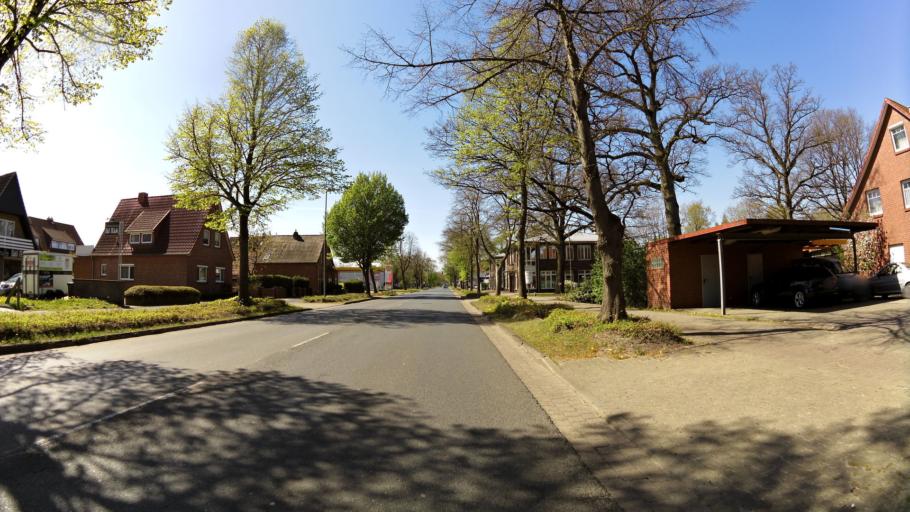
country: DE
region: Lower Saxony
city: Rotenburg
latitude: 53.1175
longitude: 9.4197
